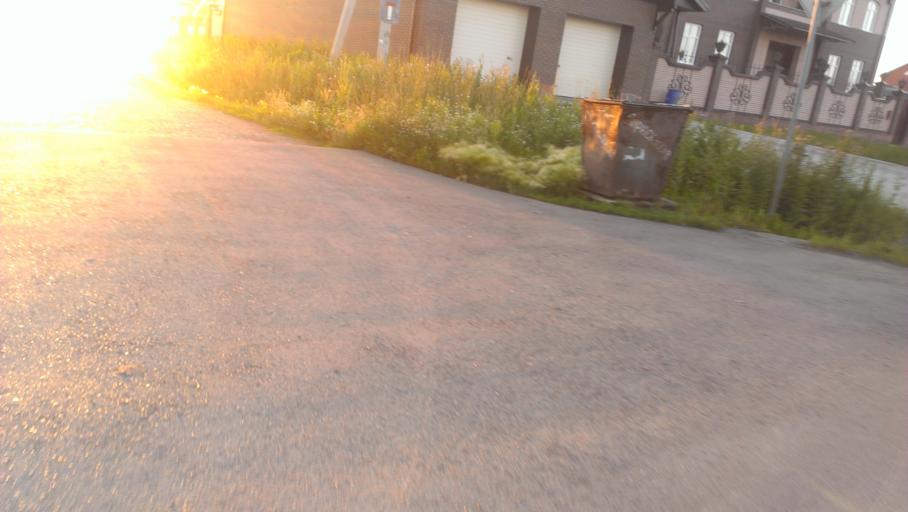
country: RU
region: Altai Krai
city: Novosilikatnyy
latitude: 53.3700
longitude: 83.6511
